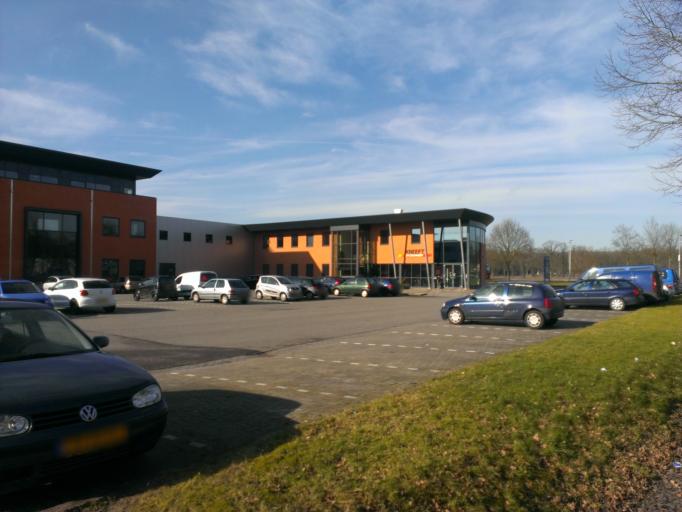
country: NL
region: Drenthe
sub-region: Gemeente Hoogeveen
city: Hoogeveen
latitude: 52.7388
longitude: 6.4729
